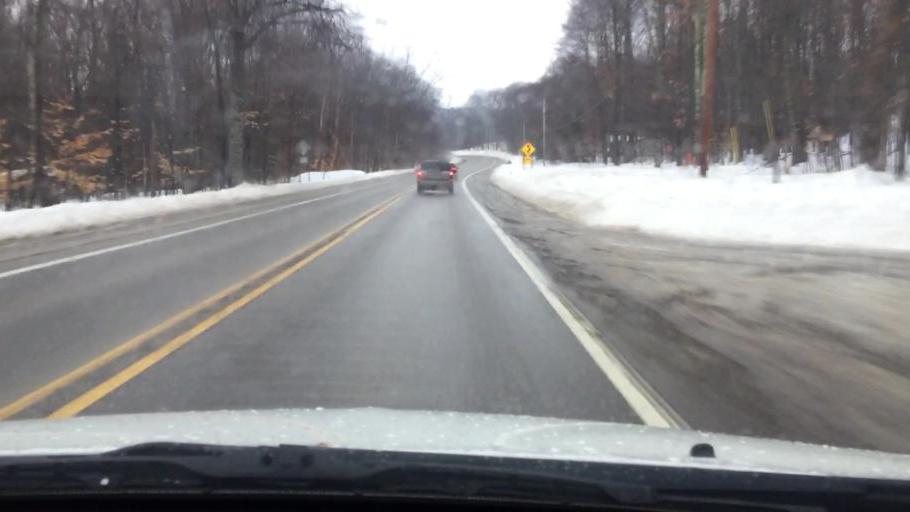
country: US
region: Michigan
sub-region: Charlevoix County
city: East Jordan
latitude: 45.2167
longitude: -85.1721
